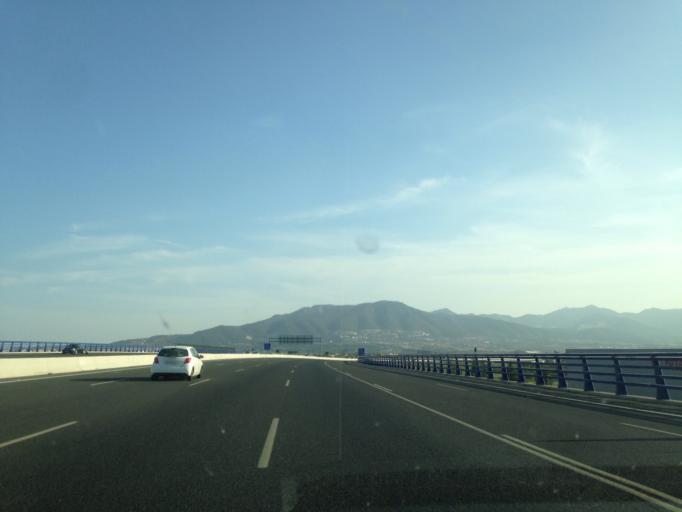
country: ES
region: Andalusia
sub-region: Provincia de Malaga
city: Alhaurin de la Torre
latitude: 36.7043
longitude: -4.5147
